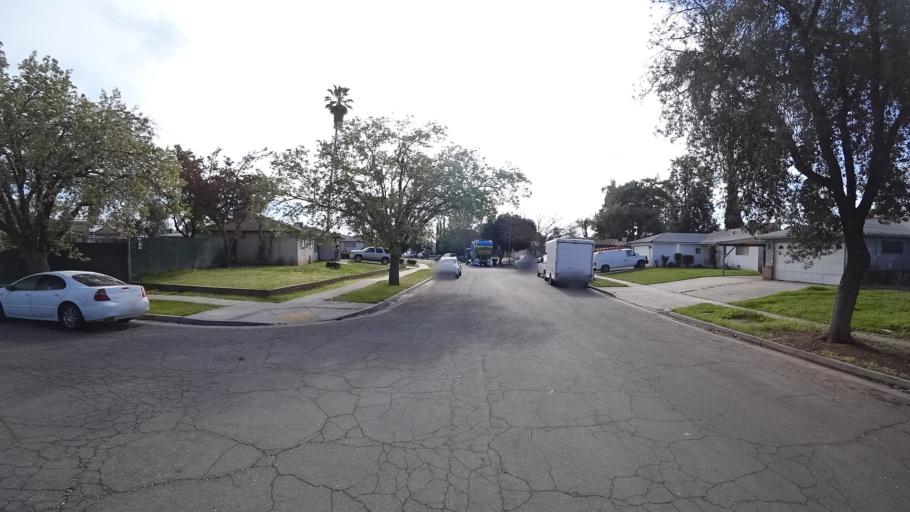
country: US
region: California
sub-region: Fresno County
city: Fresno
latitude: 36.8037
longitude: -119.8463
